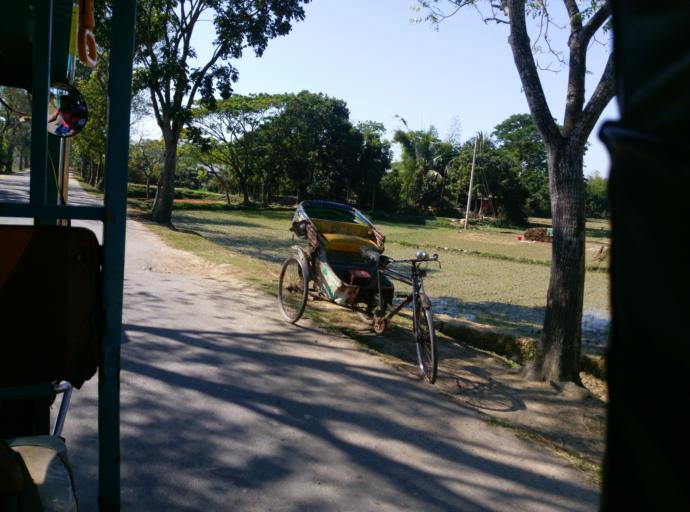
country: BD
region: Dhaka
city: Netrakona
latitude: 25.0673
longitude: 90.5007
